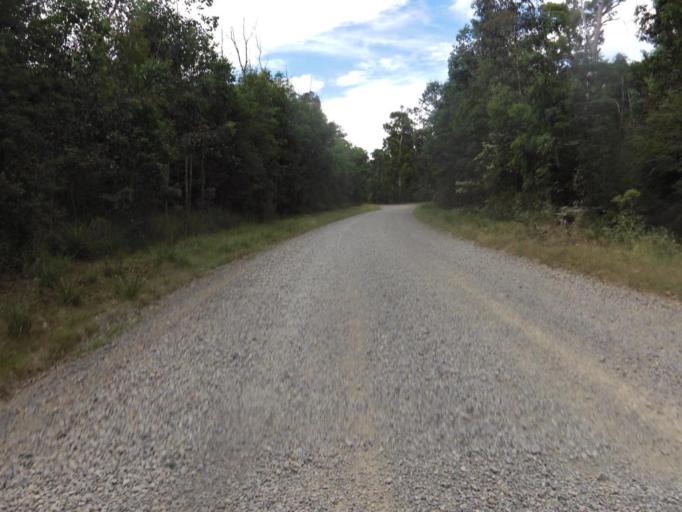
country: AU
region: Victoria
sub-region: Murrindindi
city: Alexandra
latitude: -37.3990
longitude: 145.5591
